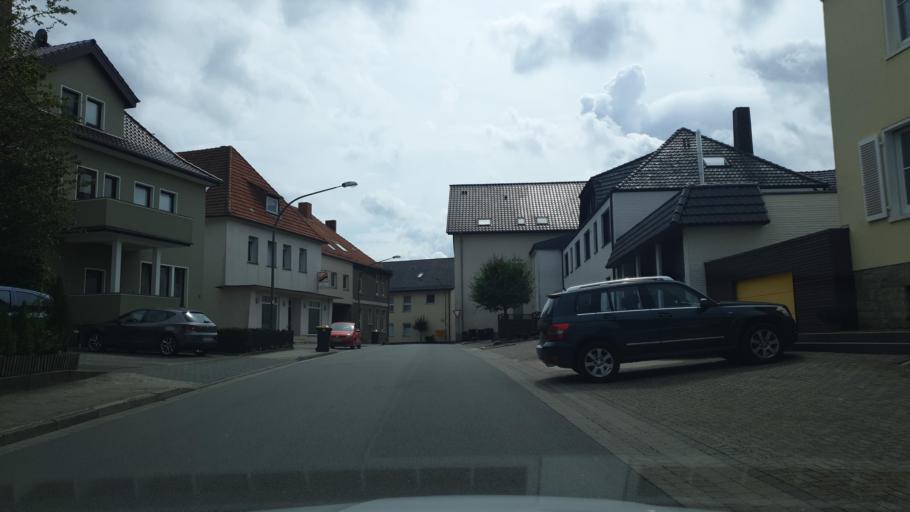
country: DE
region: Lower Saxony
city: Bissendorf
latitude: 52.1908
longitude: 8.1829
